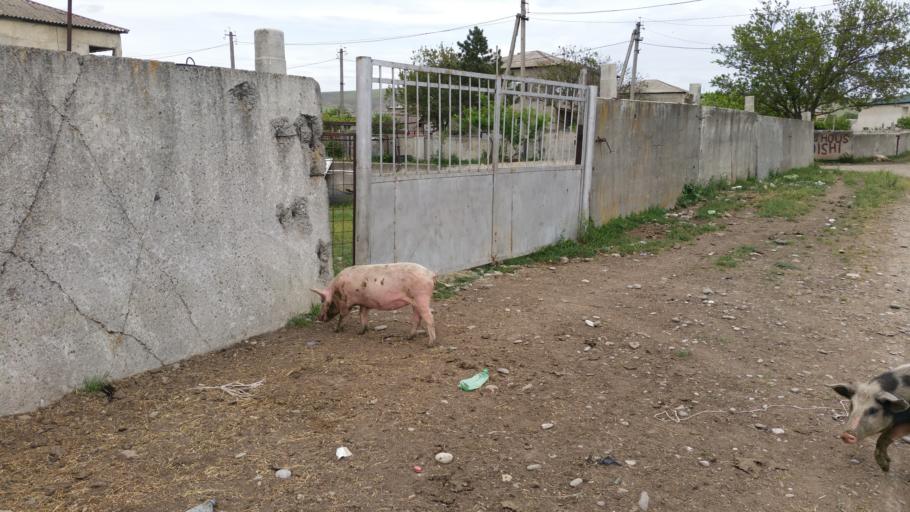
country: AZ
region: Agstafa
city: Saloglu
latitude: 41.5011
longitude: 45.3790
